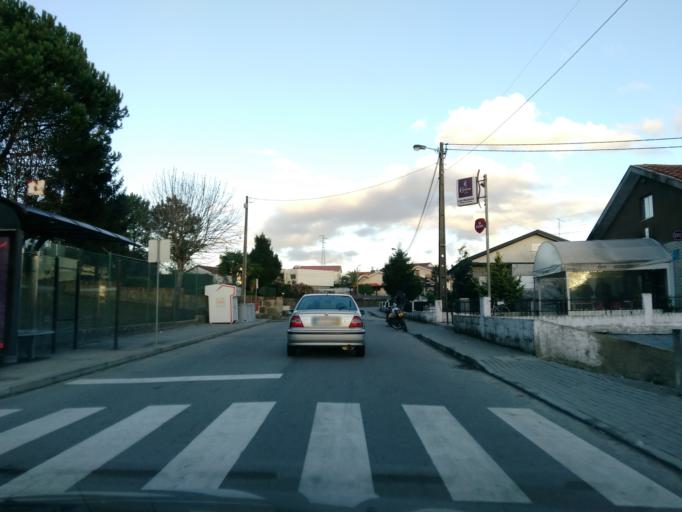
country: PT
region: Braga
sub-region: Braga
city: Braga
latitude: 41.5284
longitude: -8.4570
